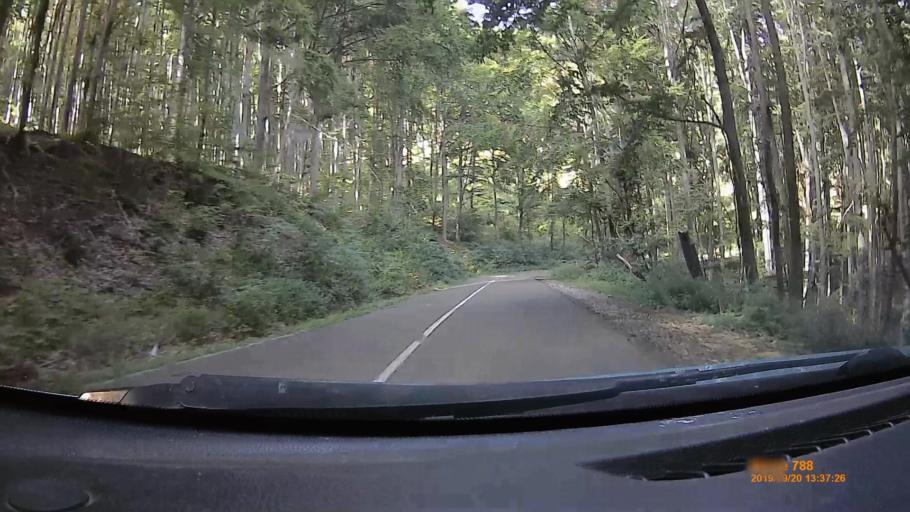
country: HU
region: Heves
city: Szilvasvarad
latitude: 48.0597
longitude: 20.5178
